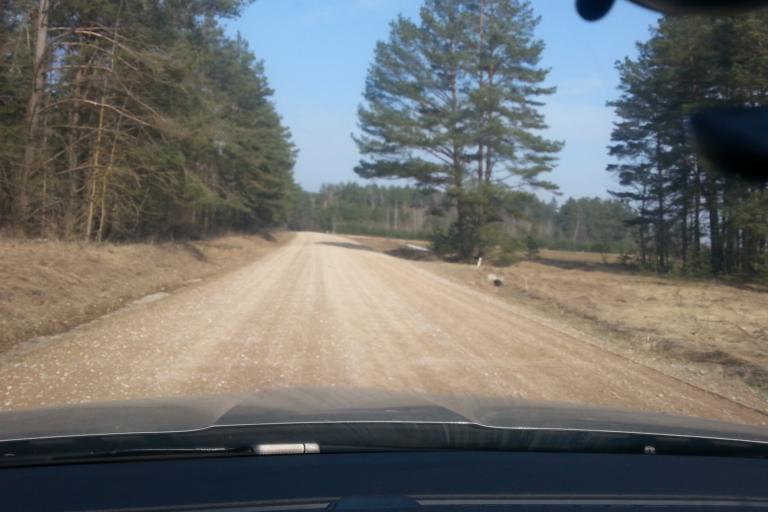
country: LT
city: Trakai
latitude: 54.5726
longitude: 24.9679
